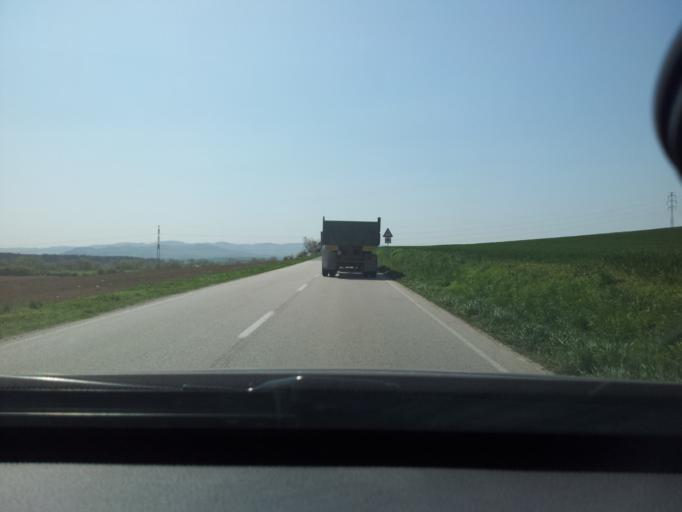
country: SK
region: Nitriansky
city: Banovce nad Bebravou
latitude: 48.6344
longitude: 18.2539
